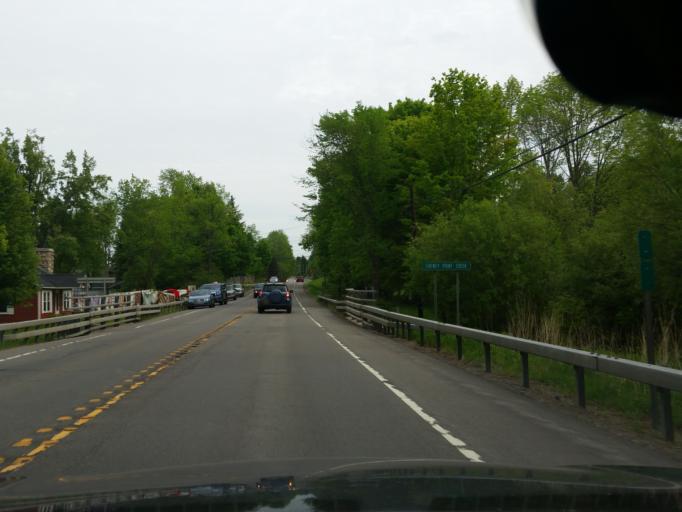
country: US
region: New York
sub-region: Chautauqua County
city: Lakewood
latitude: 42.1323
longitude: -79.3958
